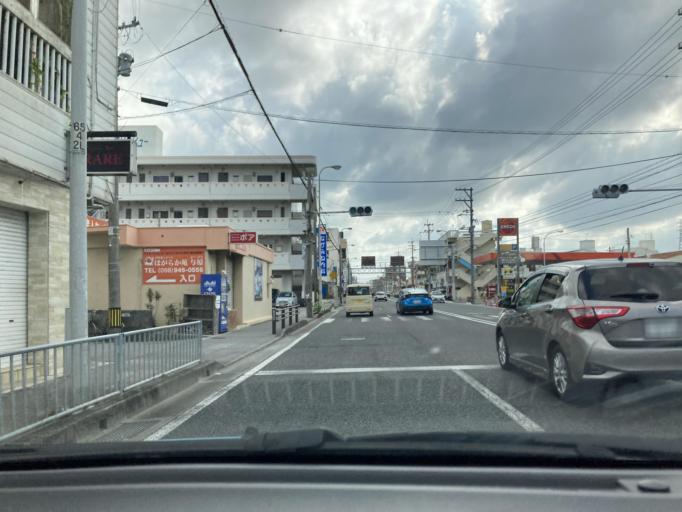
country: JP
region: Okinawa
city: Ginowan
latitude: 26.2112
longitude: 127.7597
